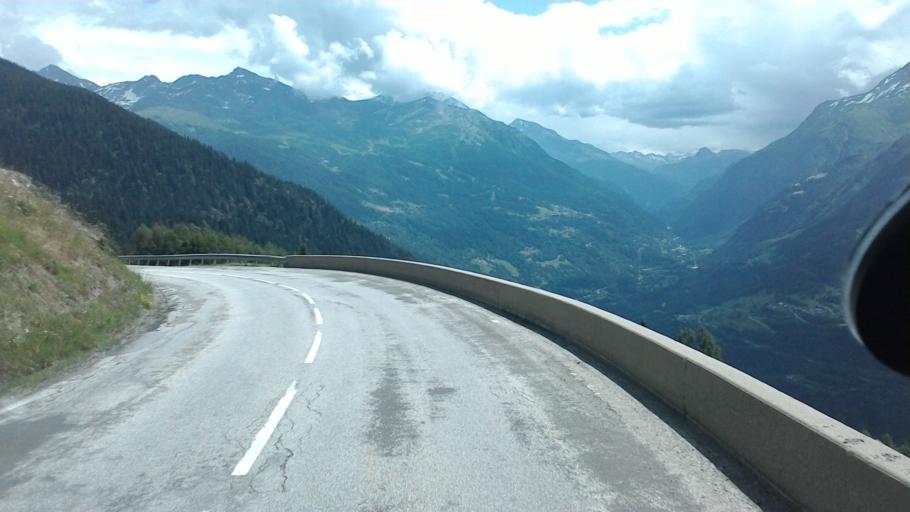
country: FR
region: Rhone-Alpes
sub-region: Departement de la Savoie
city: Seez
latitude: 45.6217
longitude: 6.8574
